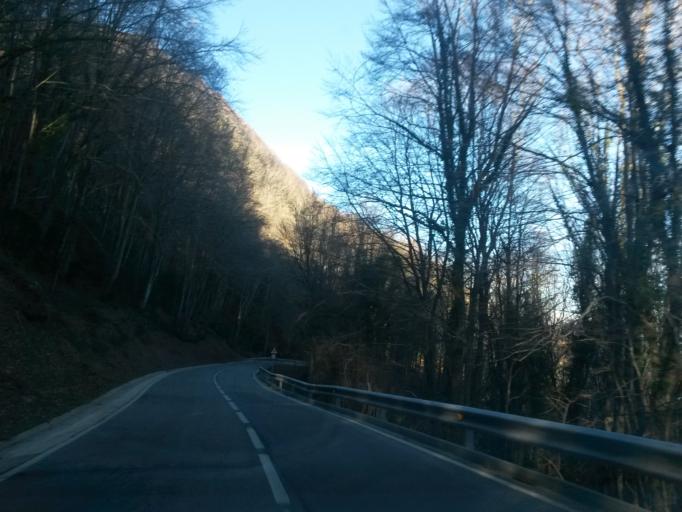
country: ES
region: Catalonia
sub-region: Provincia de Girona
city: Sant Feliu de Pallerols
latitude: 42.0511
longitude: 2.5089
